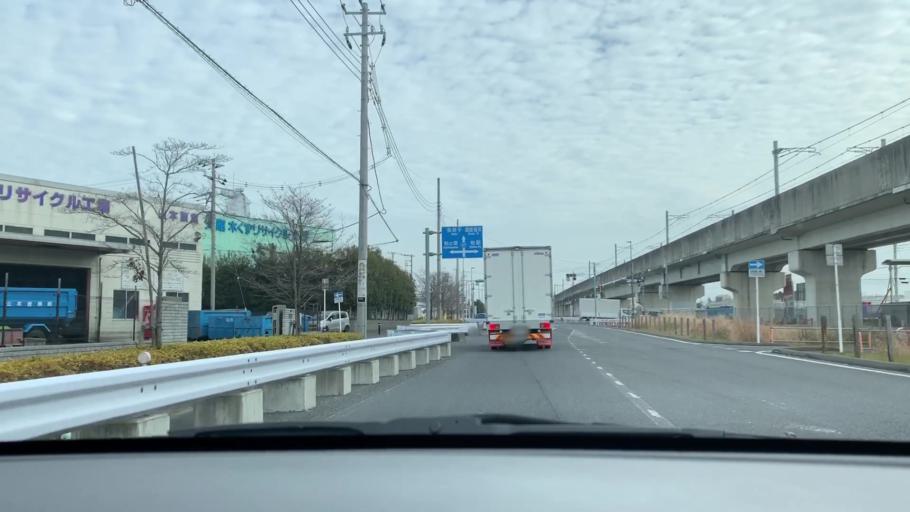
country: JP
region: Chiba
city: Kashiwa
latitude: 35.8849
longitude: 139.9435
